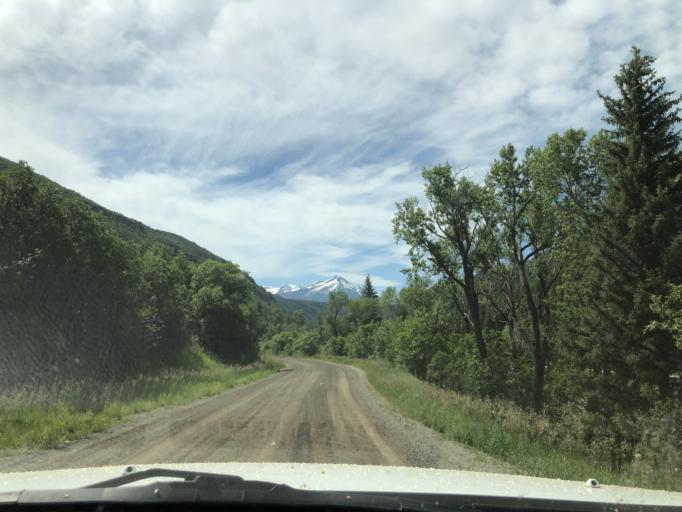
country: US
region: Colorado
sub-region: Delta County
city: Paonia
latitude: 38.9916
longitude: -107.3499
